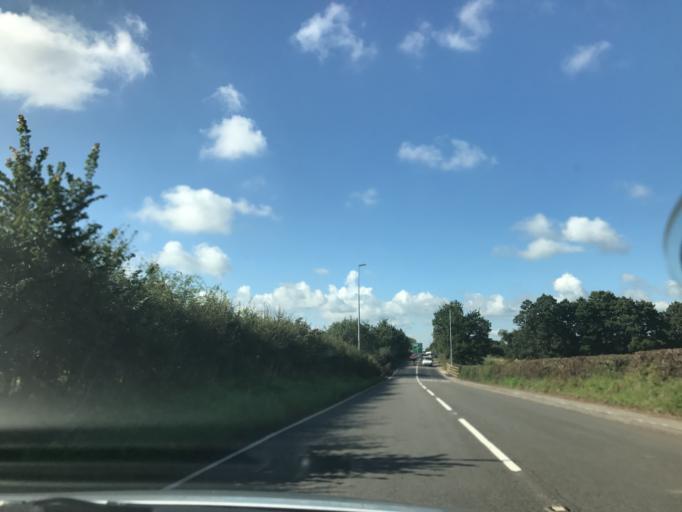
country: GB
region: England
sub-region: Cheshire East
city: Nantwich
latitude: 53.0809
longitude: -2.5056
